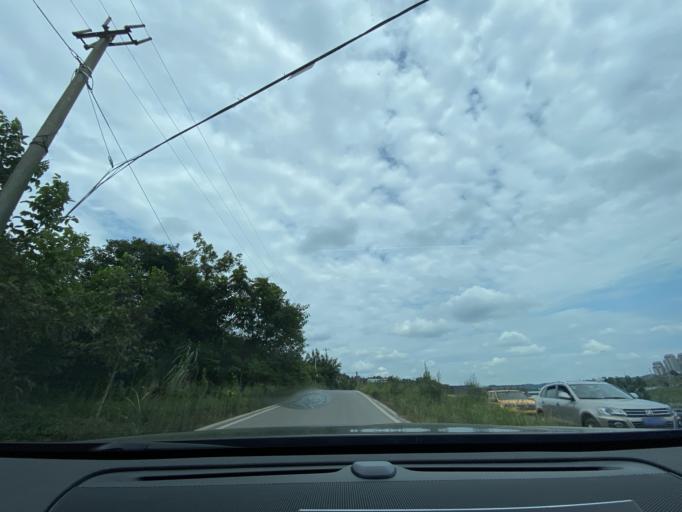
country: CN
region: Sichuan
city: Jiancheng
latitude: 30.4360
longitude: 104.5284
